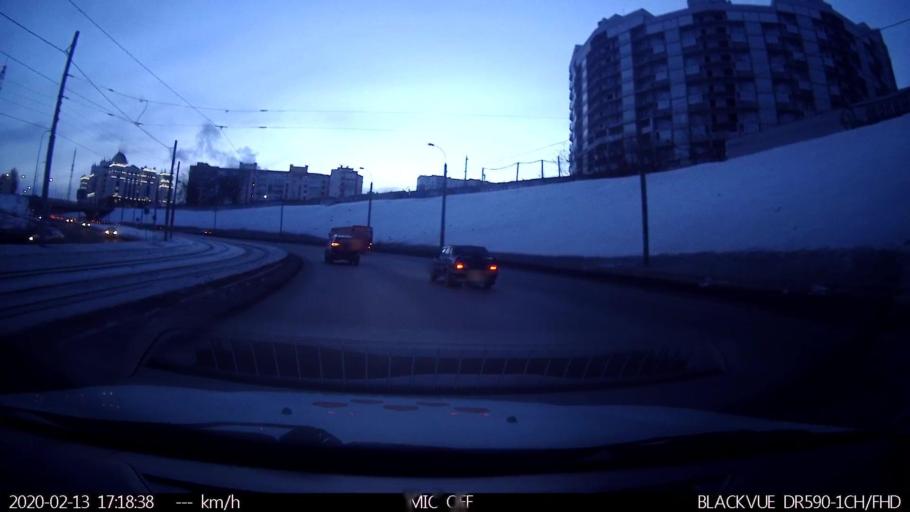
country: RU
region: Nizjnij Novgorod
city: Nizhniy Novgorod
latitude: 56.3062
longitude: 43.9706
